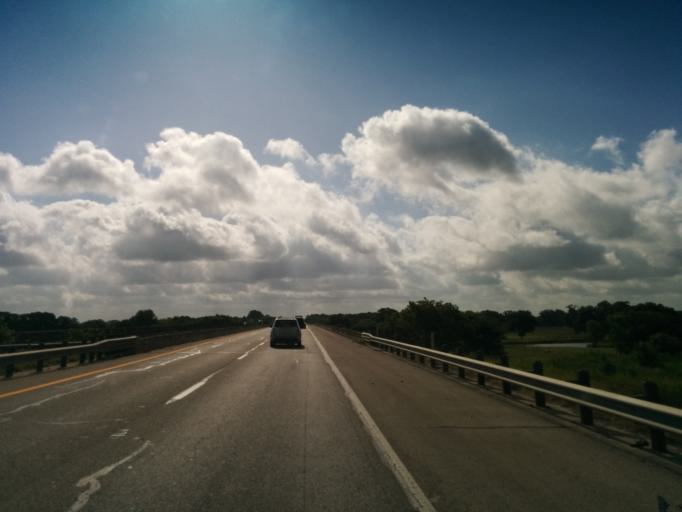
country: US
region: Texas
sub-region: Caldwell County
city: Luling
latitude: 29.6498
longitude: -97.6434
